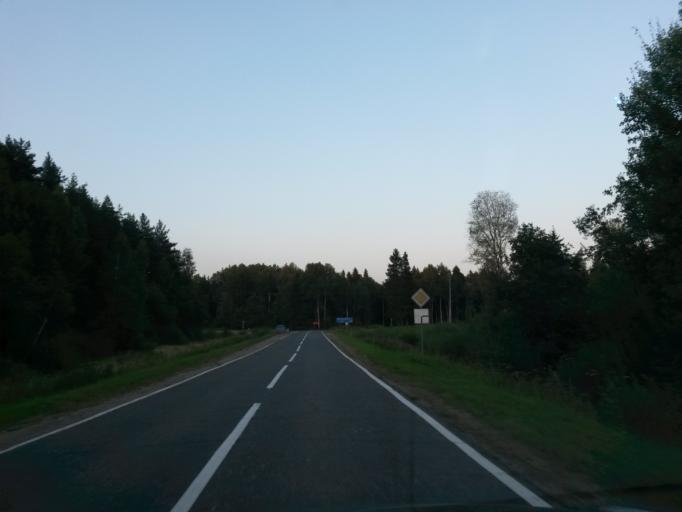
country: RU
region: Jaroslavl
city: Tutayev
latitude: 57.9488
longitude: 39.4955
